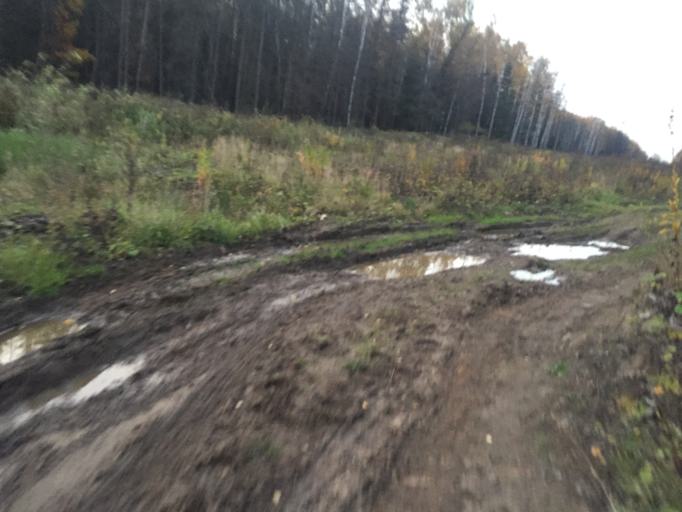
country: RU
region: Moskovskaya
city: Druzhba
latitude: 55.8703
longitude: 37.7674
